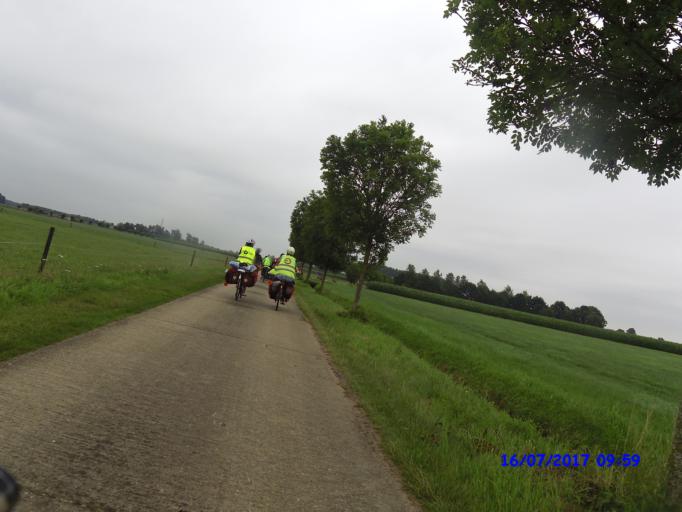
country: BE
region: Flanders
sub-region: Provincie Antwerpen
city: Lille
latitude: 51.2250
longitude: 4.8639
